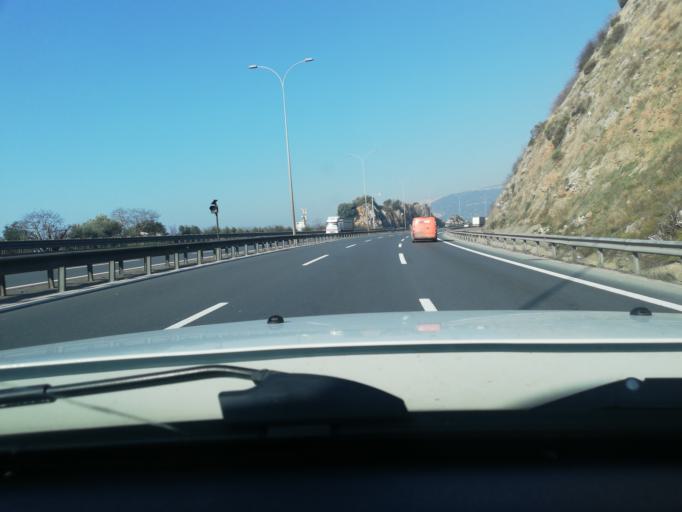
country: TR
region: Kocaeli
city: Hereke
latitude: 40.7772
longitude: 29.6343
